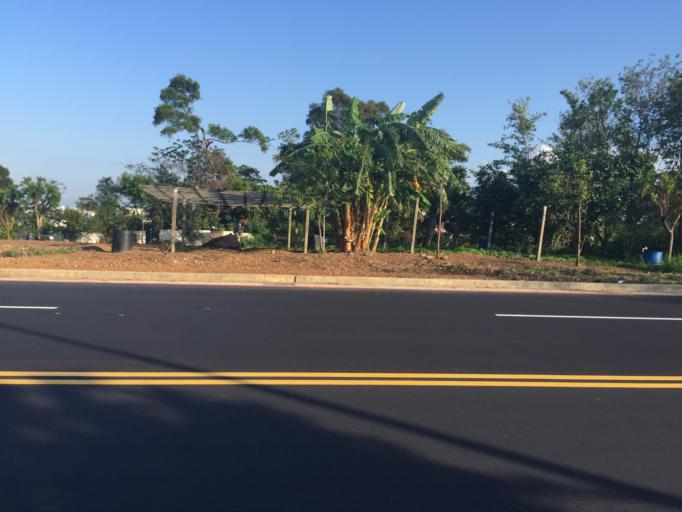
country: TW
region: Taiwan
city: Taoyuan City
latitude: 24.9410
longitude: 121.2641
